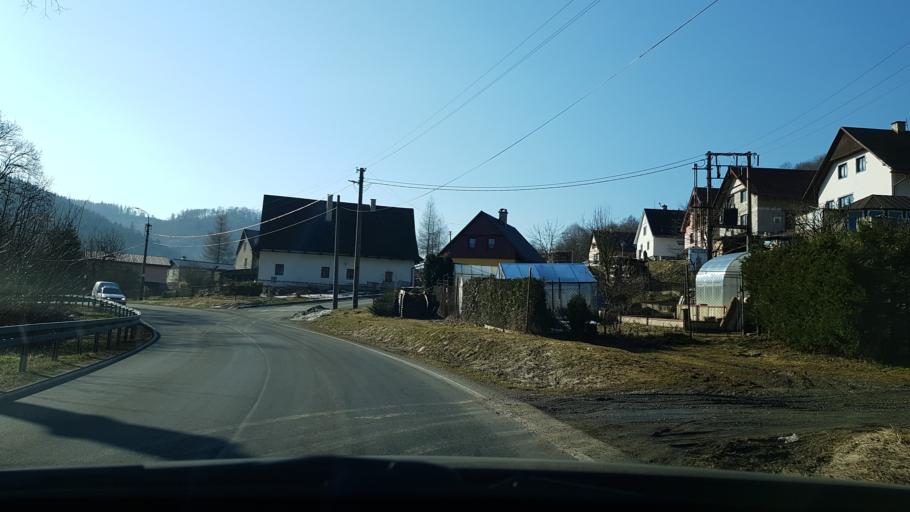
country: CZ
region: Olomoucky
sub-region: Okres Sumperk
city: Hanusovice
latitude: 50.0641
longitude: 16.9236
